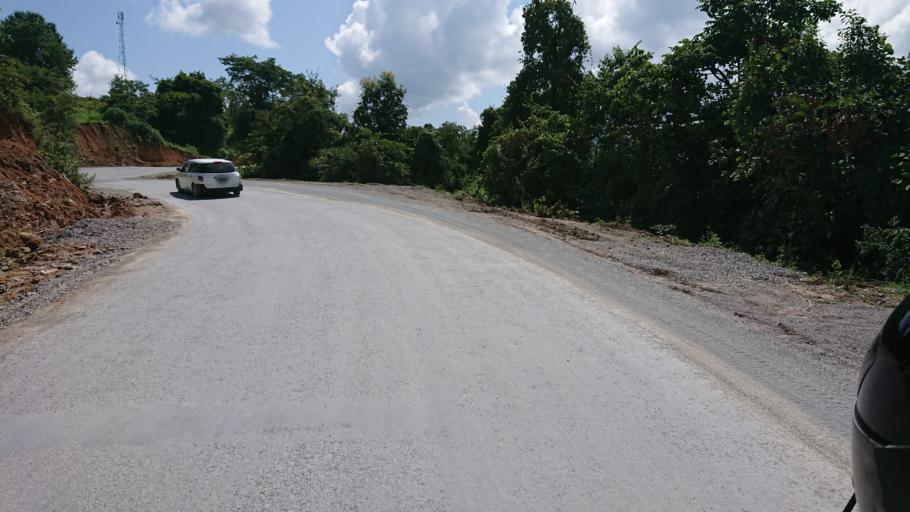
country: MM
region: Shan
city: Taunggyi
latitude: 20.8127
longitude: 97.3203
